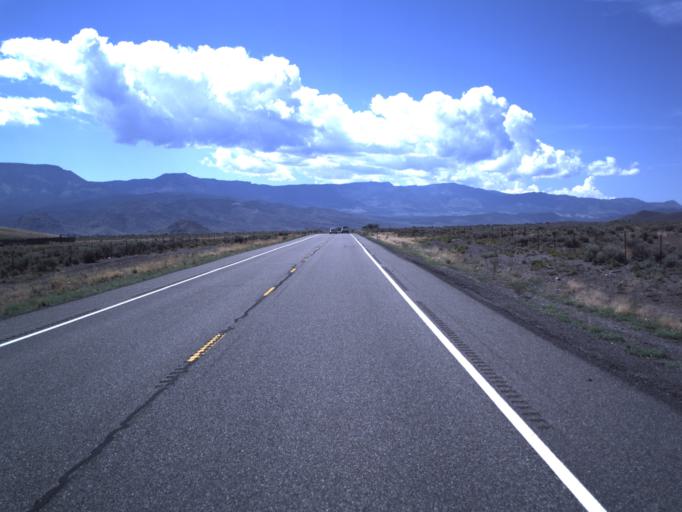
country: US
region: Utah
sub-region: Piute County
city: Junction
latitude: 38.2655
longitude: -112.2218
